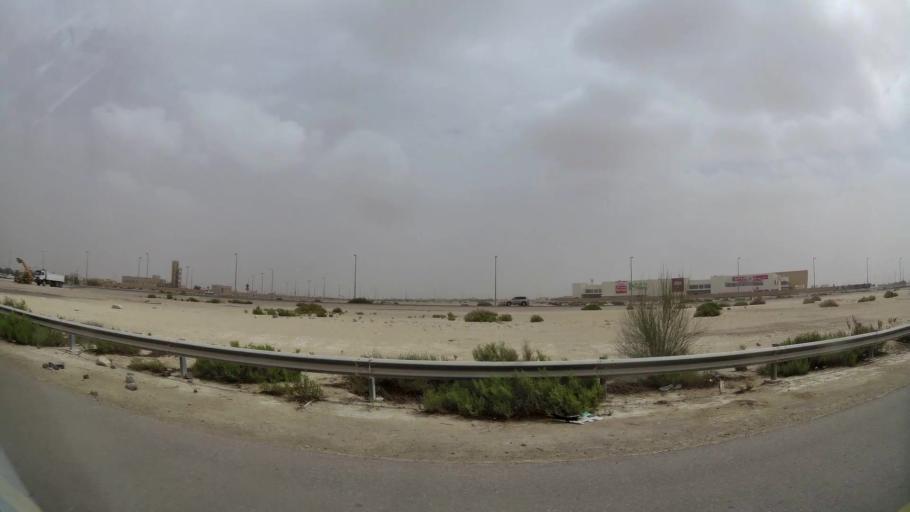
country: AE
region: Abu Dhabi
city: Abu Dhabi
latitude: 24.3889
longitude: 54.7190
